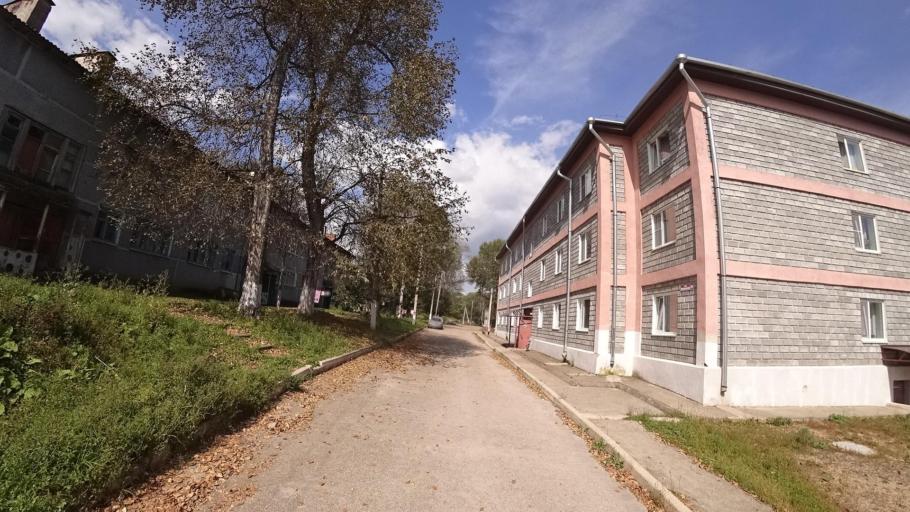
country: RU
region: Jewish Autonomous Oblast
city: Londoko
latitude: 49.0237
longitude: 131.9226
